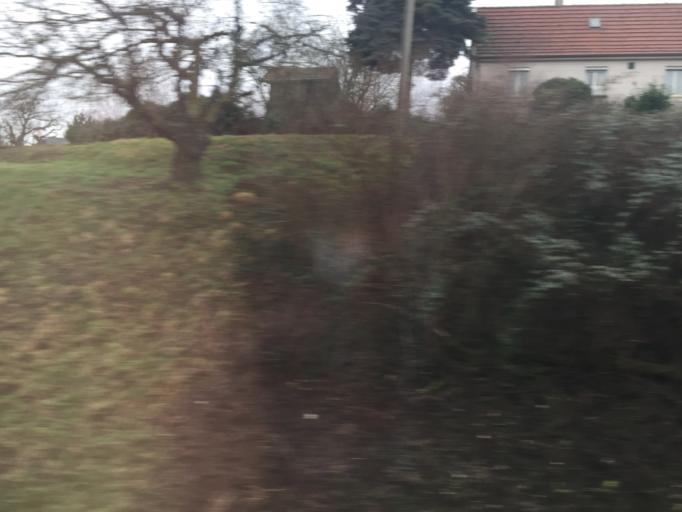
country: DE
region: Baden-Wuerttemberg
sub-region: Regierungsbezirk Stuttgart
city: Besigheim
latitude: 48.9928
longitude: 9.1436
